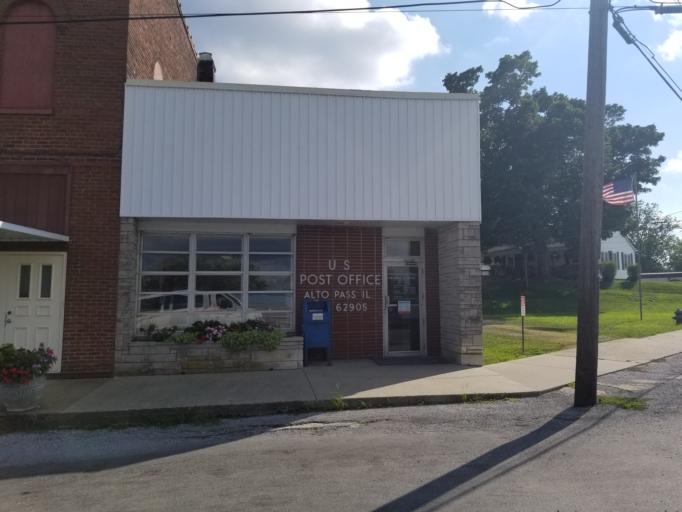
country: US
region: Illinois
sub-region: Union County
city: Cobden
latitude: 37.5704
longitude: -89.3187
